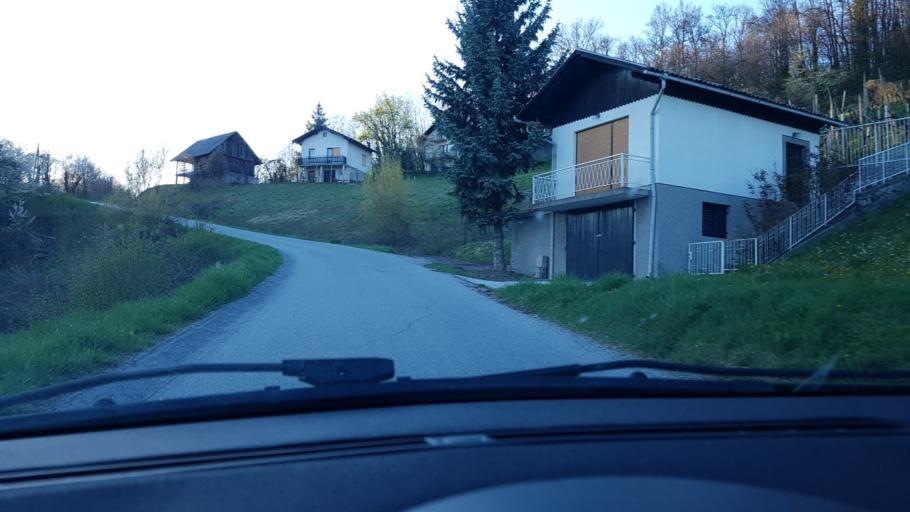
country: HR
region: Krapinsko-Zagorska
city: Pregrada
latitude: 46.1666
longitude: 15.7042
